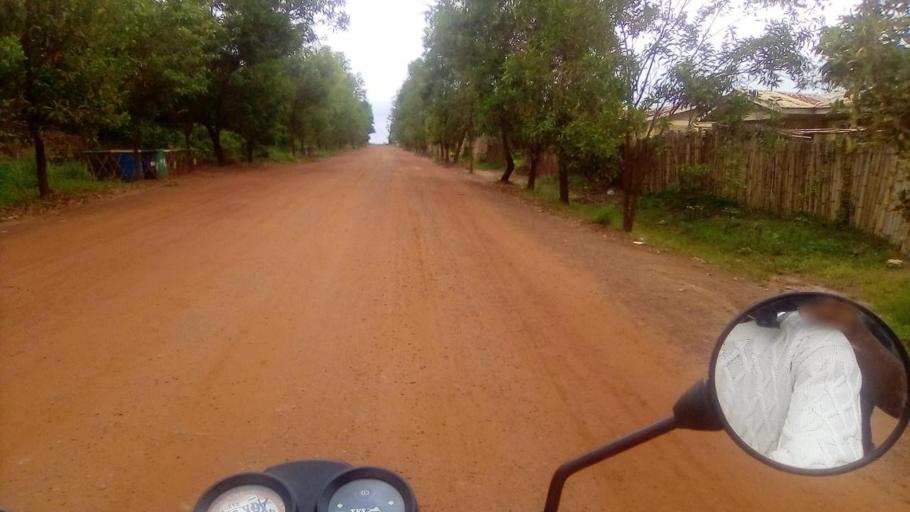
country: SL
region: Southern Province
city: Tongole
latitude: 7.4346
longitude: -11.8451
